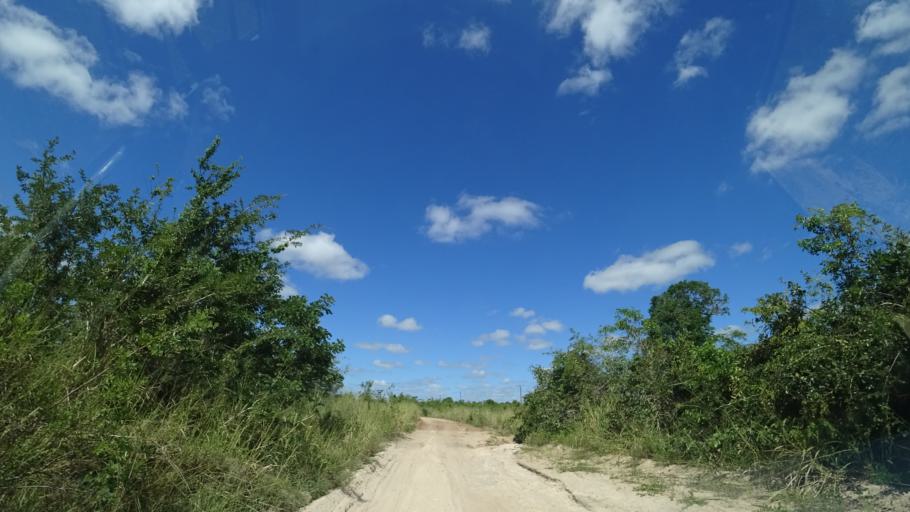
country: MZ
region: Sofala
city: Dondo
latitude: -19.2989
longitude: 34.6908
